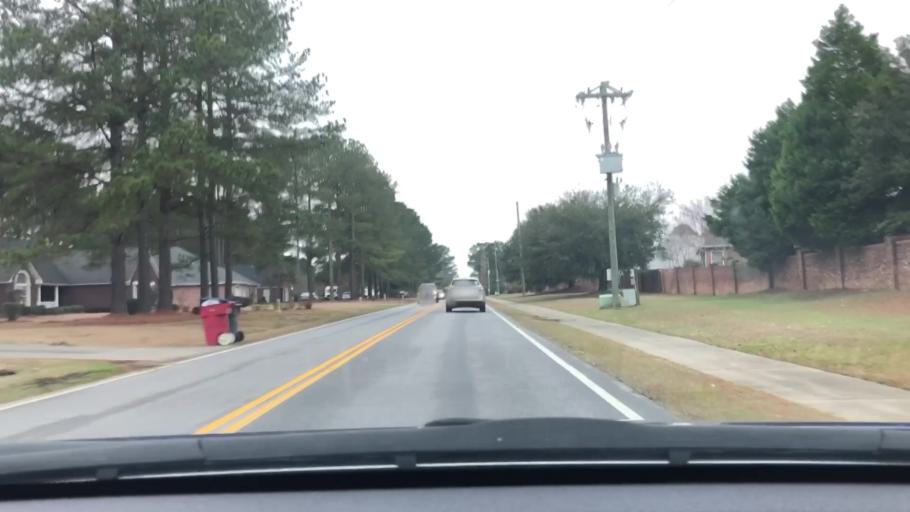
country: US
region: South Carolina
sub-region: Sumter County
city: Cherryvale
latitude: 33.9355
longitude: -80.4092
